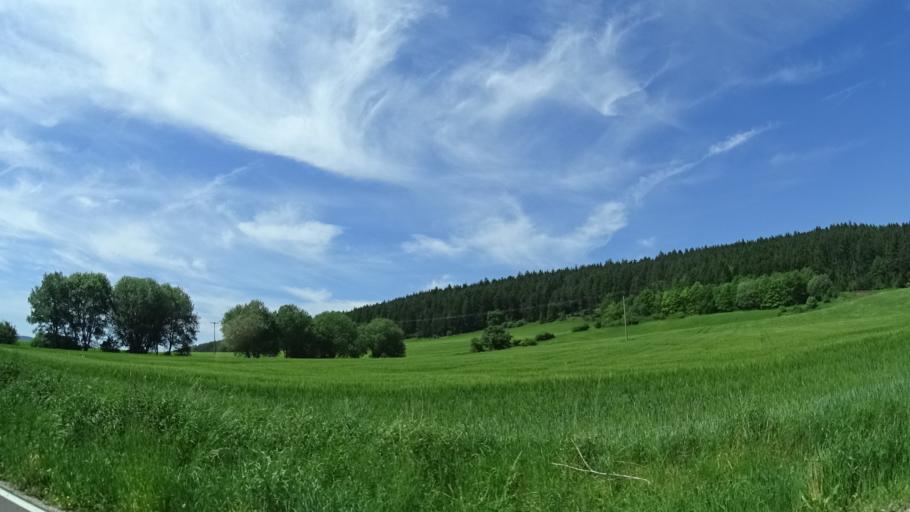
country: DE
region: Thuringia
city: Plaue
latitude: 50.7455
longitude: 10.9413
